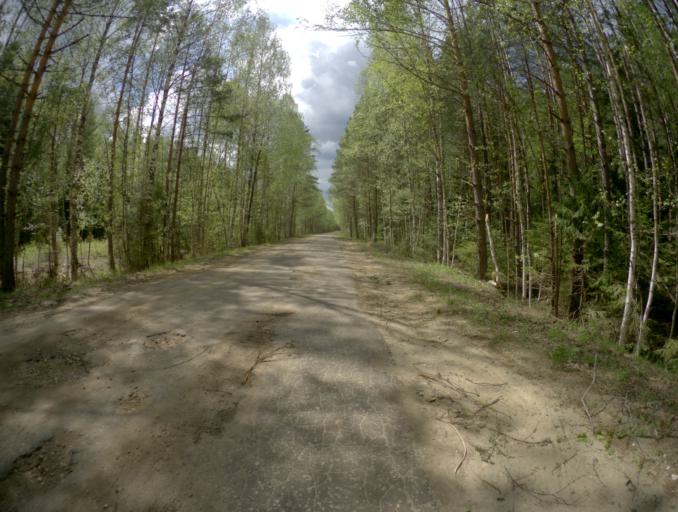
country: RU
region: Vladimir
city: Velikodvorskiy
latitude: 55.2454
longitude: 40.7504
